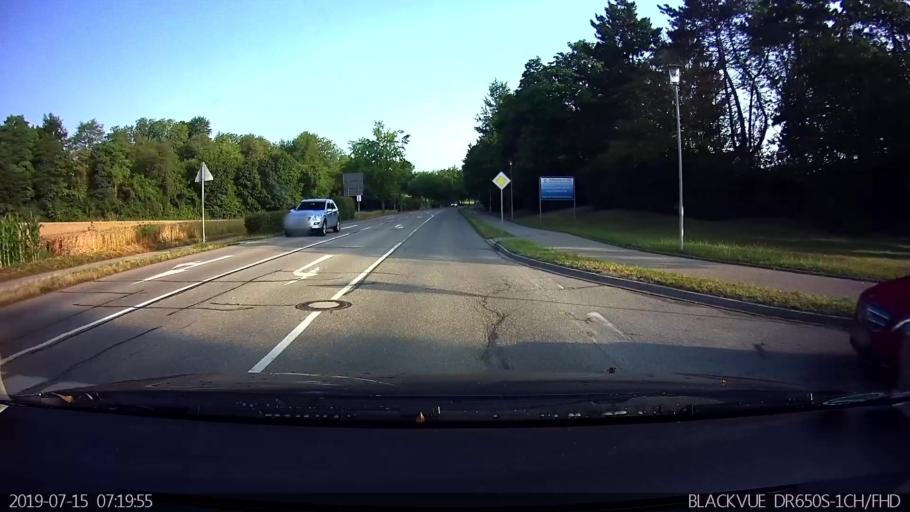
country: DE
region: Baden-Wuerttemberg
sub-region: Freiburg Region
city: Unterkrozingen
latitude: 47.9174
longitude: 7.6879
